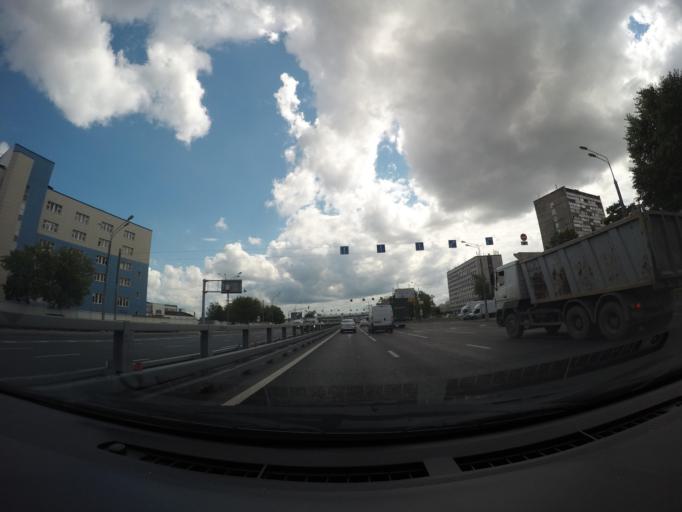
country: RU
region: Moscow
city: Veshnyaki
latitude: 55.7094
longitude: 37.8279
